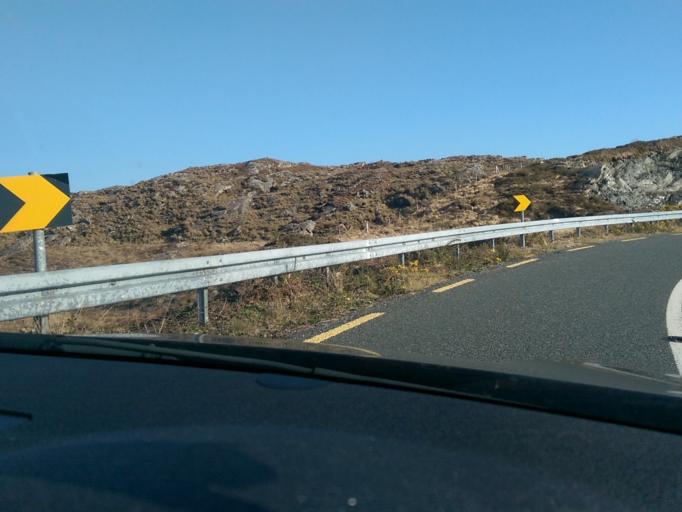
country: IE
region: Connaught
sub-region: County Galway
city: Clifden
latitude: 53.4057
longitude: -9.7827
